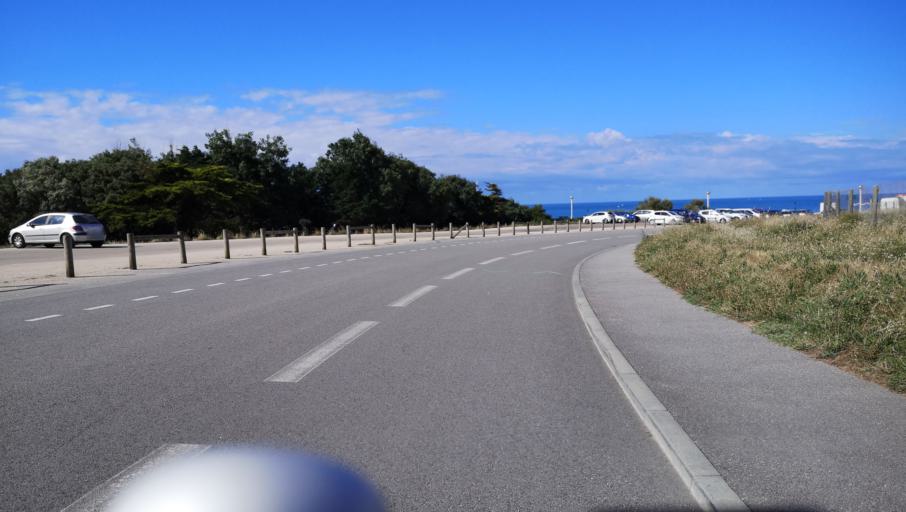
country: FR
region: Pays de la Loire
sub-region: Departement de la Vendee
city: Les Sables-d'Olonne
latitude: 46.4852
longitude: -1.7635
